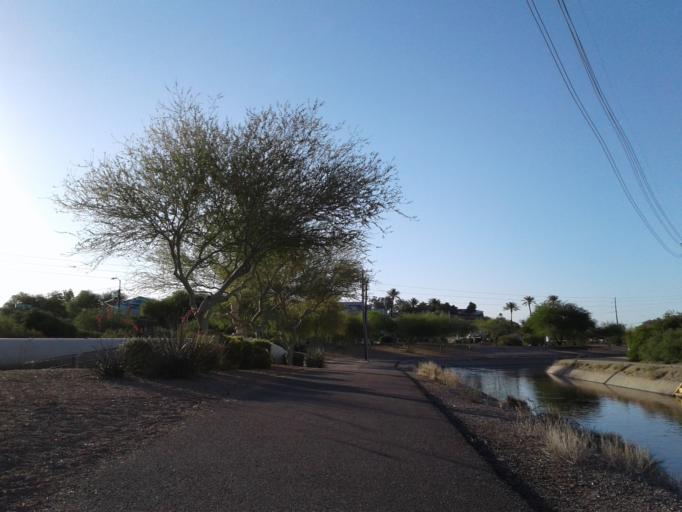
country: US
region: Arizona
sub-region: Maricopa County
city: Paradise Valley
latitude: 33.5261
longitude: -112.0311
